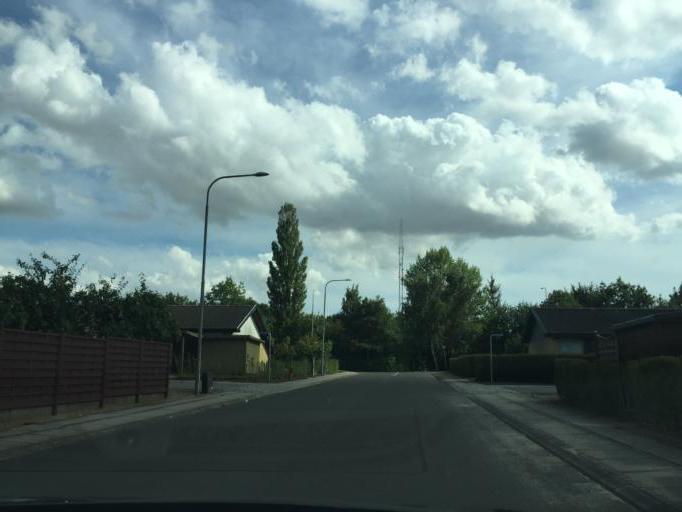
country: DK
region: South Denmark
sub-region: Odense Kommune
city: Odense
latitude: 55.3505
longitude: 10.3840
